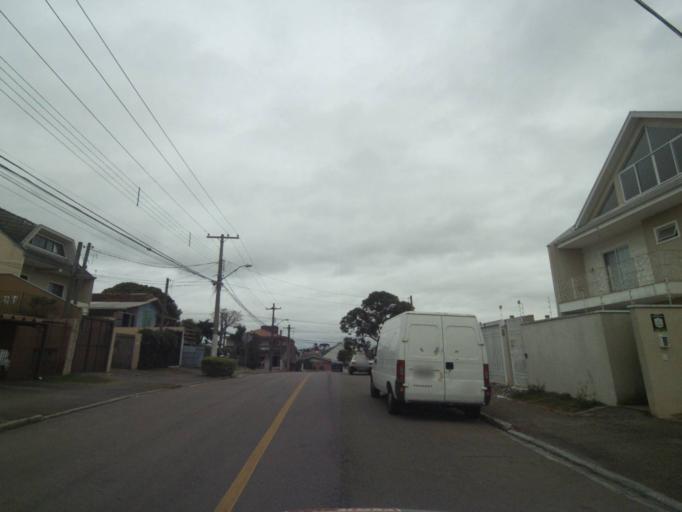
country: BR
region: Parana
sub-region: Pinhais
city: Pinhais
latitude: -25.4813
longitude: -49.2299
